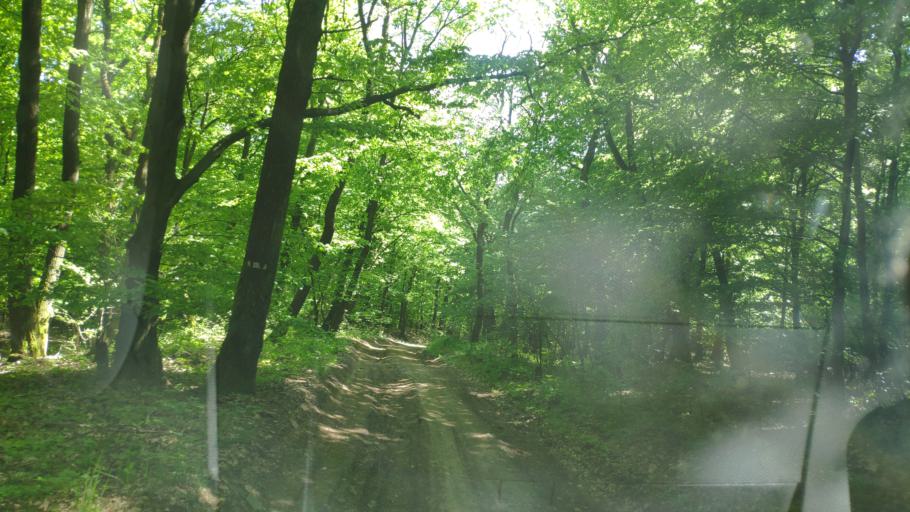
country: SK
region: Kosicky
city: Secovce
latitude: 48.7036
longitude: 21.5868
